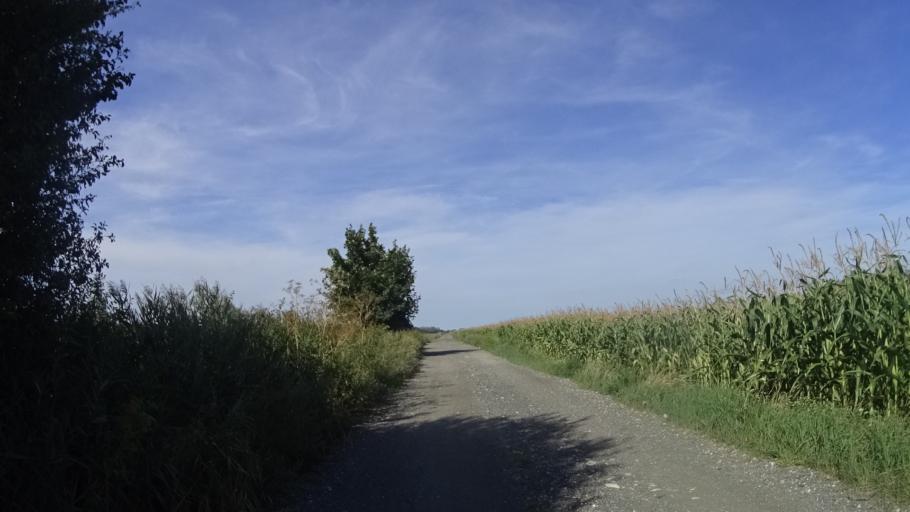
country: AT
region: Lower Austria
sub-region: Politischer Bezirk Ganserndorf
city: Durnkrut
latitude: 48.4487
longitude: 16.8833
